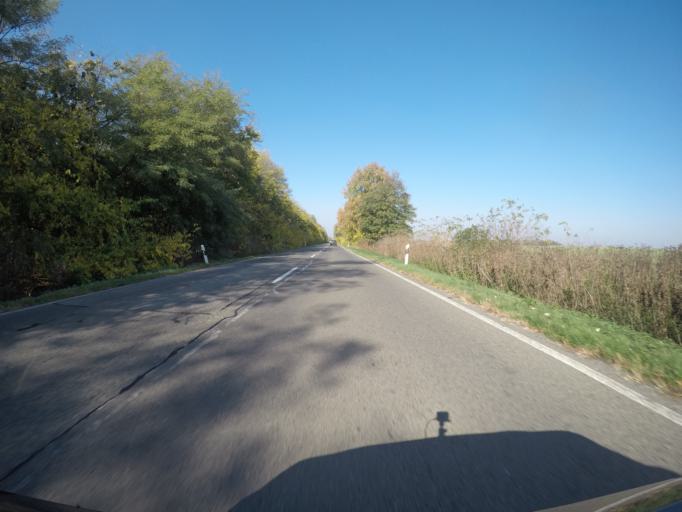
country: HU
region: Tolna
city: Szedres
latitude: 46.5189
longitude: 18.6620
